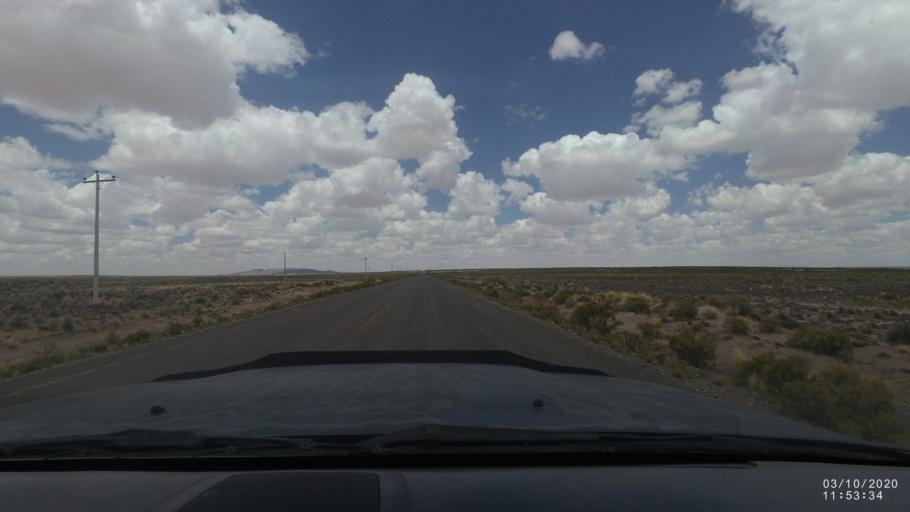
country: BO
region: Oruro
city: Poopo
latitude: -18.4813
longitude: -67.6049
